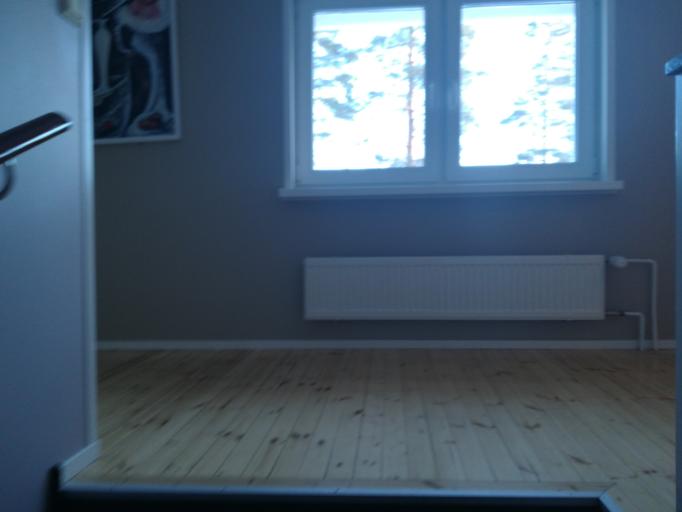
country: FI
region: Southern Savonia
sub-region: Savonlinna
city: Savonlinna
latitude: 61.8293
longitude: 29.0241
